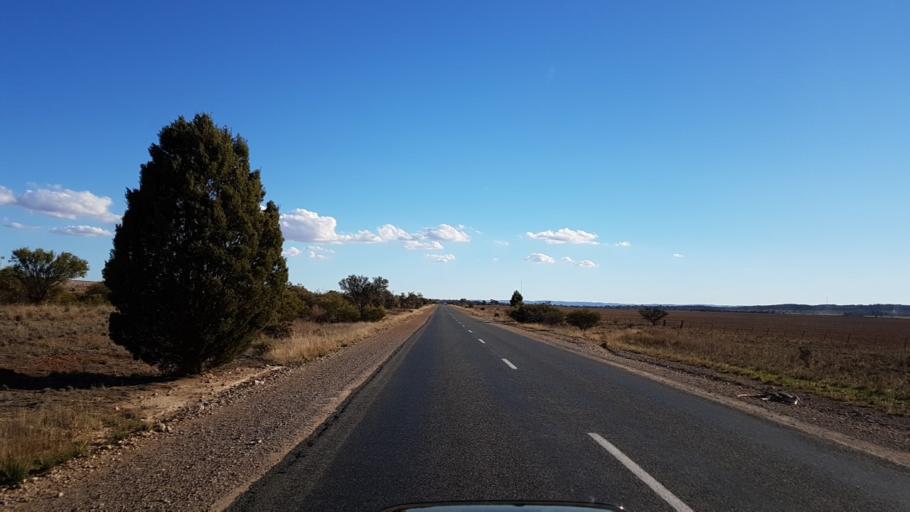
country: AU
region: South Australia
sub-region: Peterborough
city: Peterborough
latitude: -32.9630
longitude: 138.8842
